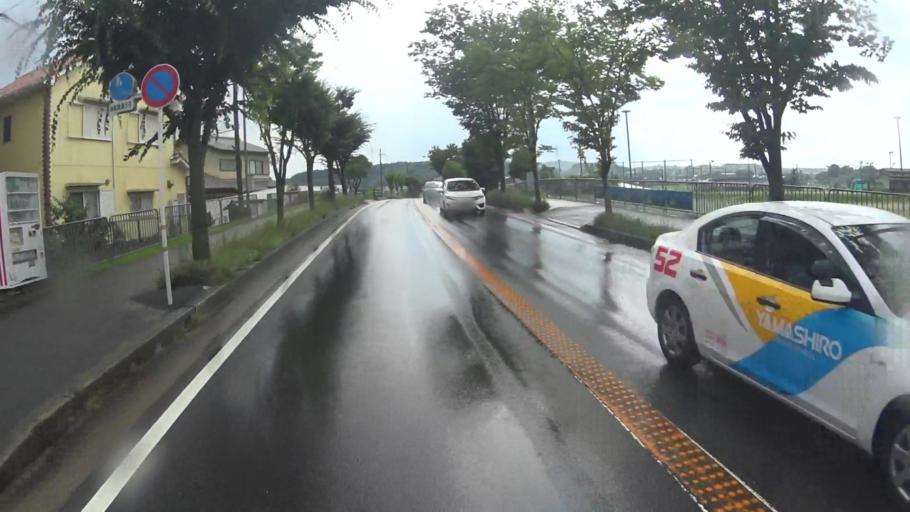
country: JP
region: Kyoto
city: Tanabe
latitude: 34.8148
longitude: 135.7800
